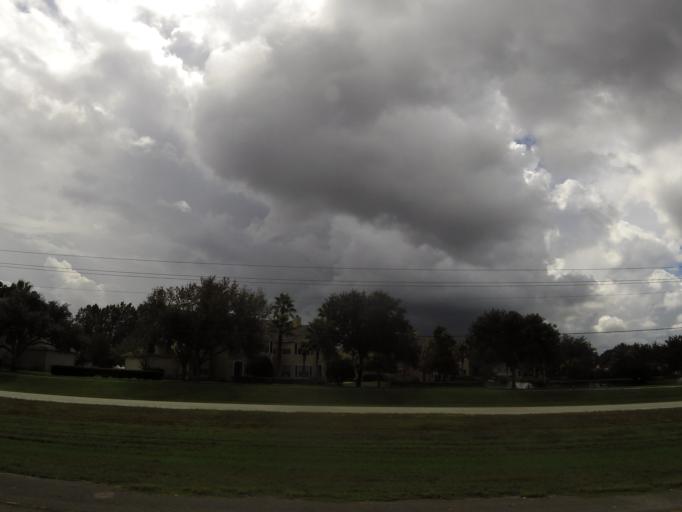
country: US
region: Florida
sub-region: Clay County
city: Lakeside
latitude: 30.1023
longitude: -81.7223
